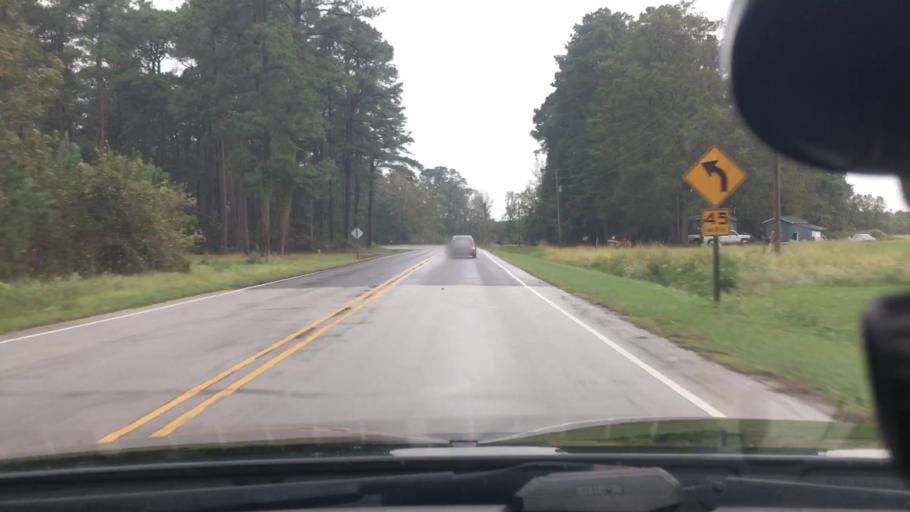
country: US
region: North Carolina
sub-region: Pitt County
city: Windsor
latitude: 35.4502
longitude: -77.2637
